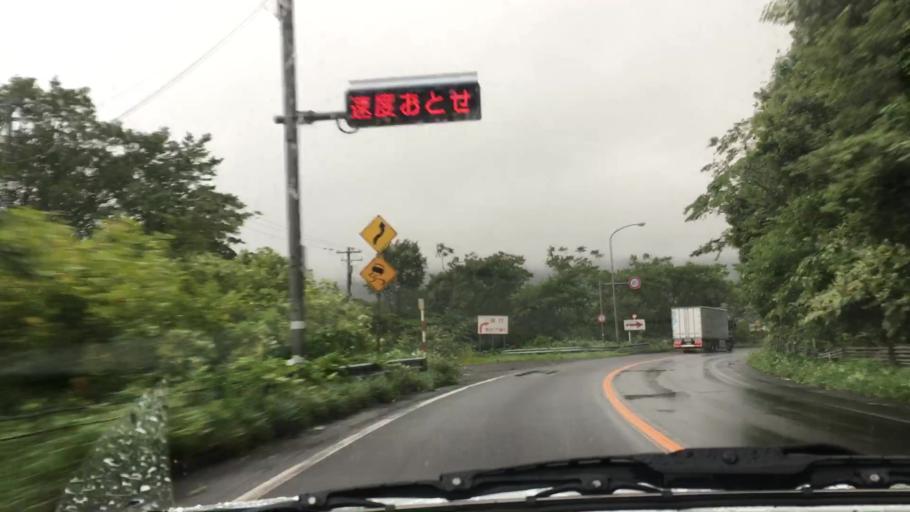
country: JP
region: Hokkaido
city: Niseko Town
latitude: 42.5916
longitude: 140.5946
